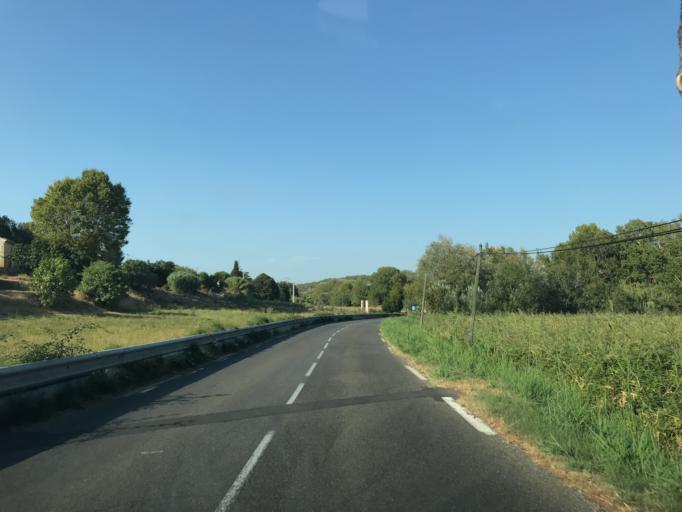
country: FR
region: Provence-Alpes-Cote d'Azur
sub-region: Departement des Bouches-du-Rhone
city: Saint-Chamas
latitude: 43.5563
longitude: 5.0132
